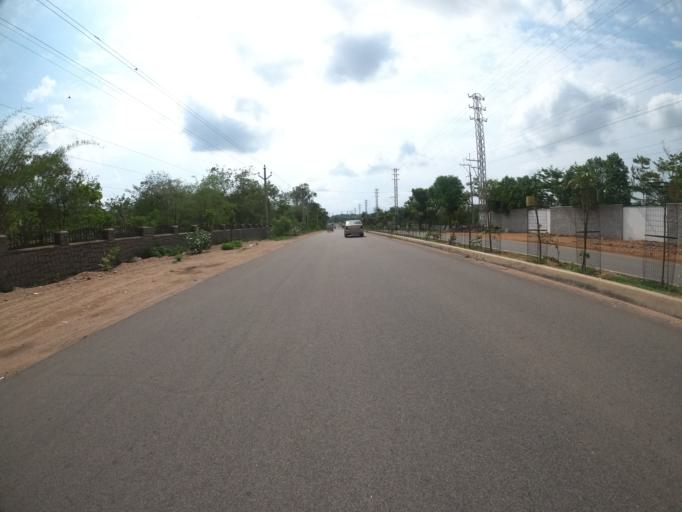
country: IN
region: Telangana
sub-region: Medak
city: Serilingampalle
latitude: 17.3924
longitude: 78.3221
